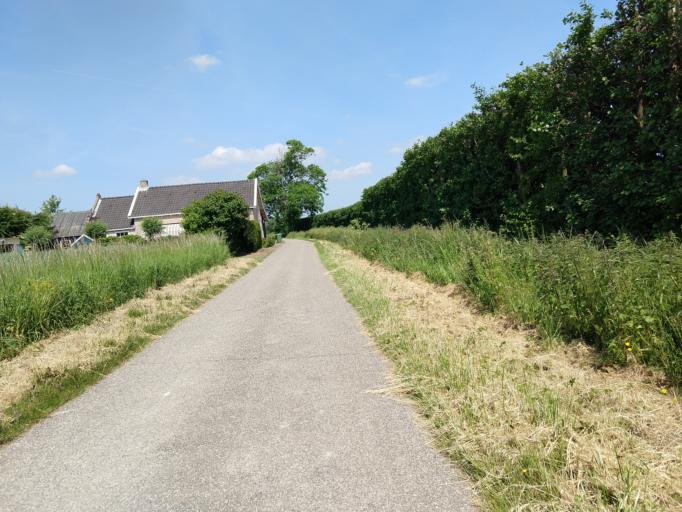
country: NL
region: Zeeland
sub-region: Gemeente Borsele
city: Borssele
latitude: 51.4348
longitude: 3.8138
